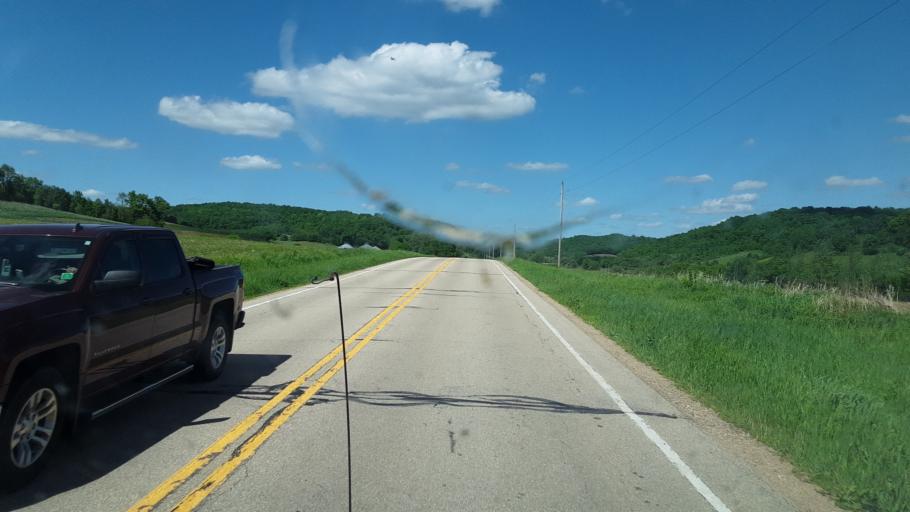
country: US
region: Wisconsin
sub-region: Richland County
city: Richland Center
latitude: 43.4466
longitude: -90.2308
